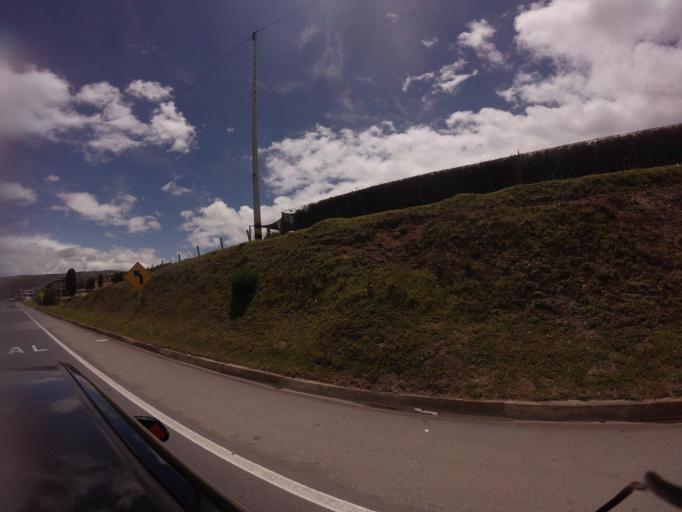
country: CO
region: Boyaca
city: Combita
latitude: 5.6257
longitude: -73.3053
